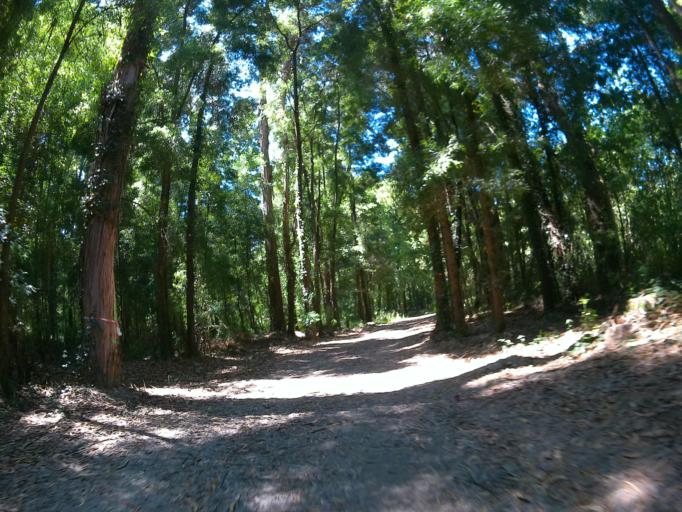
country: PT
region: Viana do Castelo
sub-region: Viana do Castelo
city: Darque
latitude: 41.7095
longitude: -8.7220
